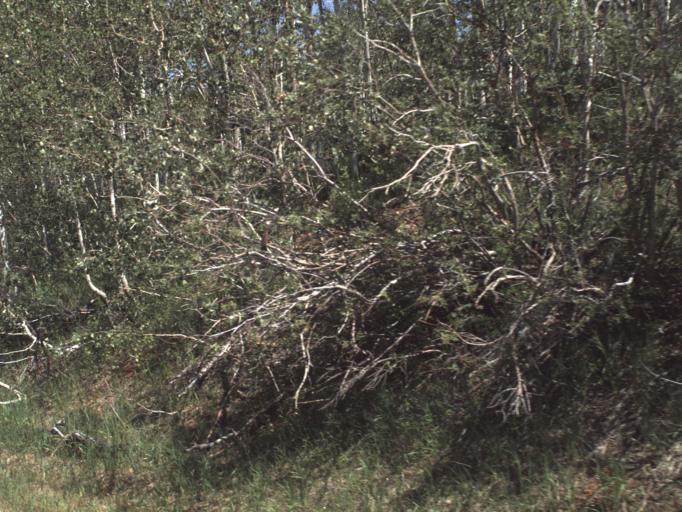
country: US
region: Utah
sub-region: Weber County
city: Wolf Creek
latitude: 41.4184
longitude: -111.5644
